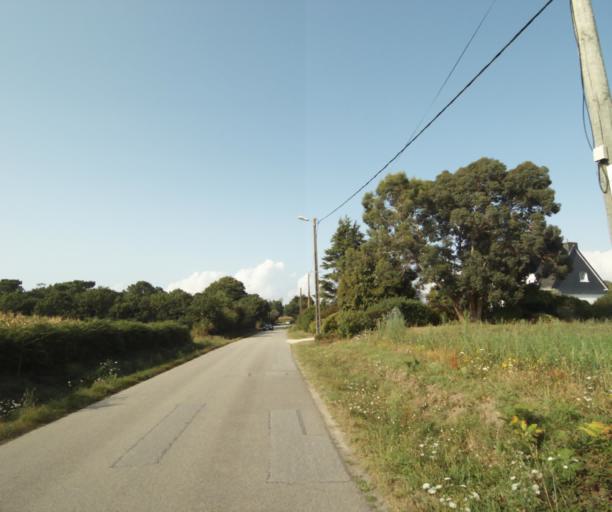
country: FR
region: Brittany
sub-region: Departement du Morbihan
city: Riantec
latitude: 47.7234
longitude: -3.2963
